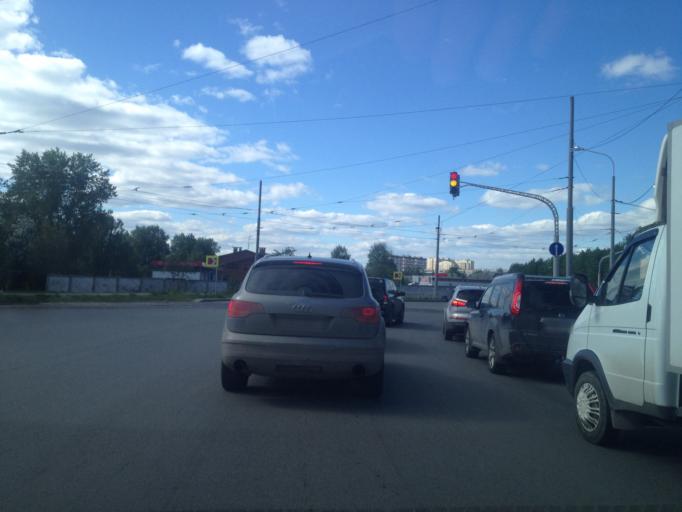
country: RU
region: Sverdlovsk
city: Shirokaya Rechka
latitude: 56.8198
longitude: 60.5366
